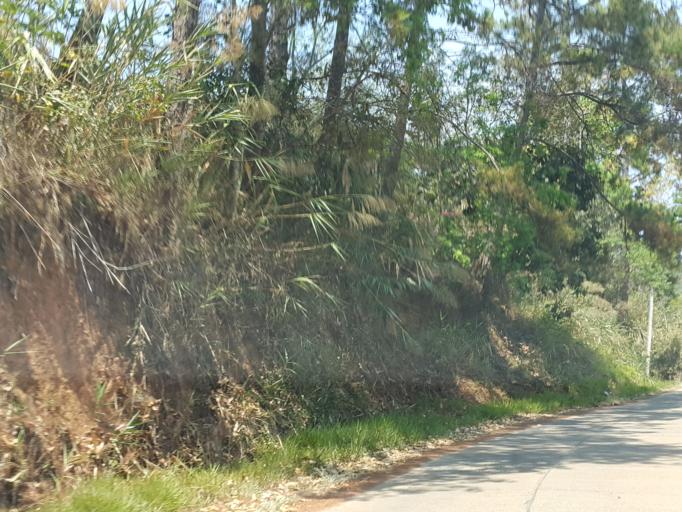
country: TH
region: Chiang Mai
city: Samoeng
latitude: 18.8830
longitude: 98.7835
